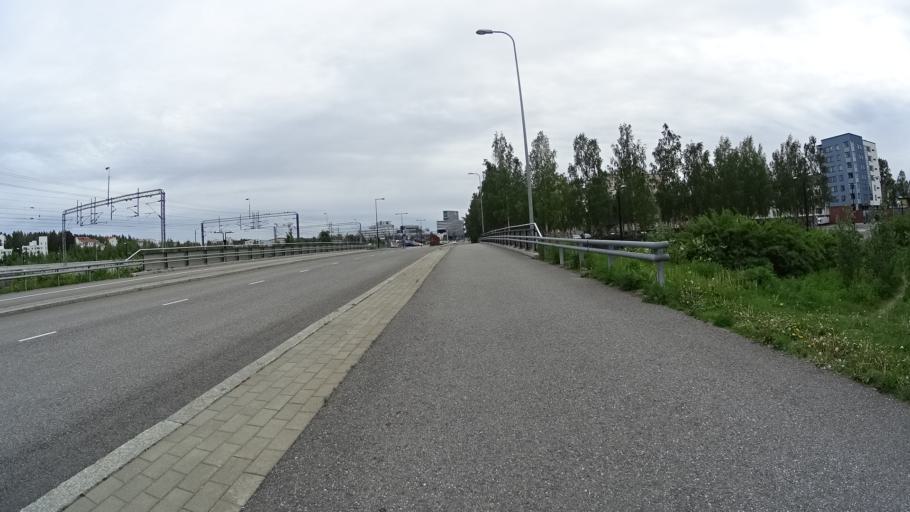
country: FI
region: Uusimaa
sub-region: Helsinki
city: Vantaa
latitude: 60.2991
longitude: 25.0470
